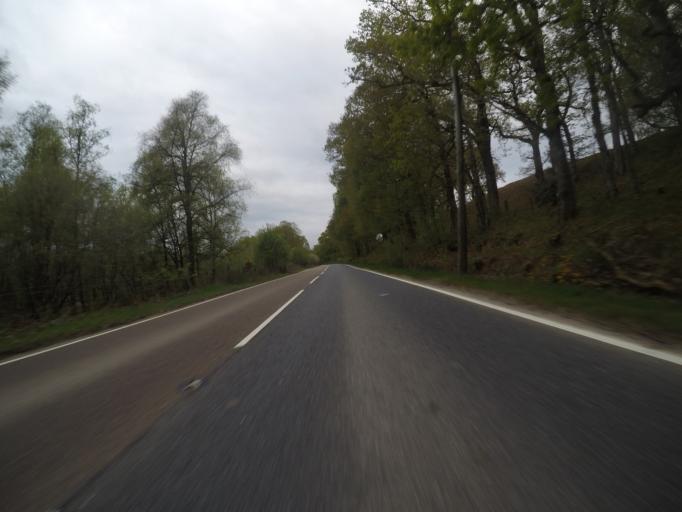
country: GB
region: Scotland
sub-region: Highland
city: Spean Bridge
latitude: 56.8943
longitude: -4.8902
